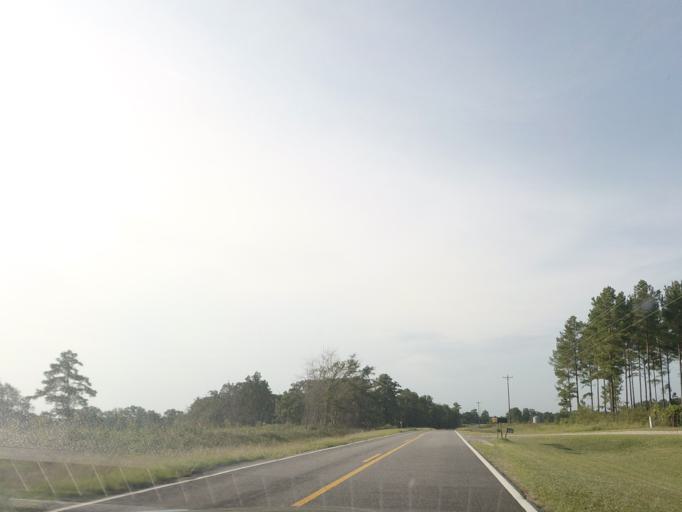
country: US
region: Georgia
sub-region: Bleckley County
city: Cochran
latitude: 32.4777
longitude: -83.3020
